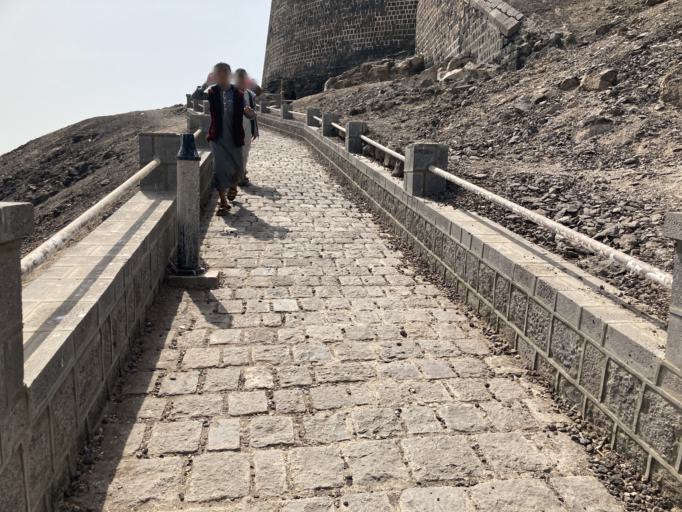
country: YE
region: Aden
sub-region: Craiter
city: Aden
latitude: 12.7794
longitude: 45.0496
